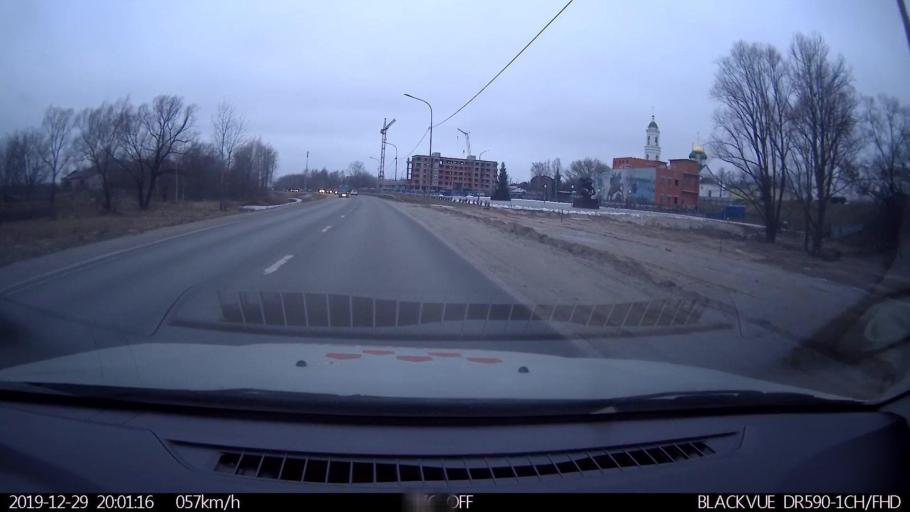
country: RU
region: Nizjnij Novgorod
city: Bor
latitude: 56.3585
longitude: 44.0461
